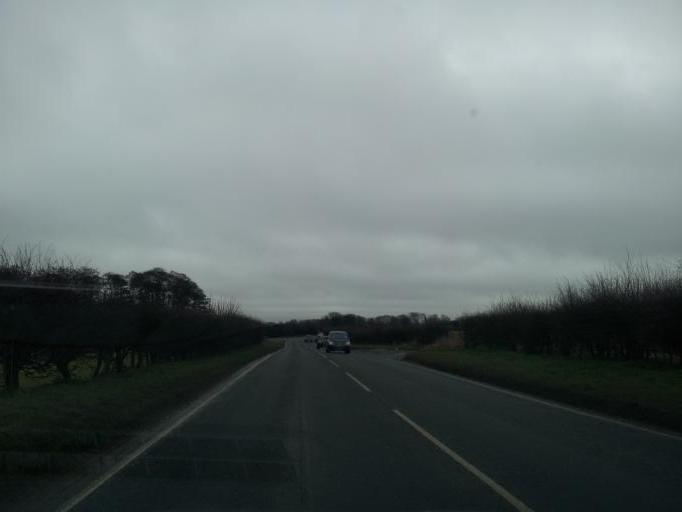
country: GB
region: England
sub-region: Essex
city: Manningtree
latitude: 51.9349
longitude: 1.0647
